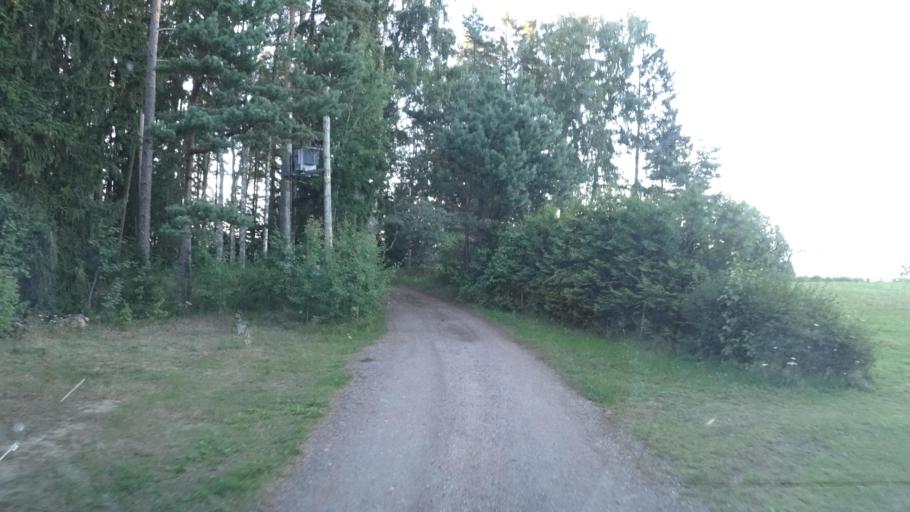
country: LV
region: Rojas
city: Roja
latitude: 57.4840
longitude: 22.8528
